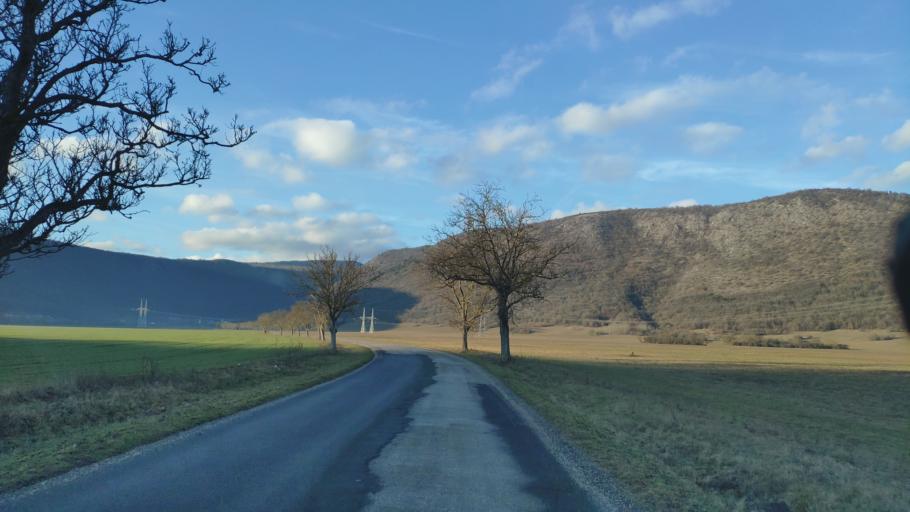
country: SK
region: Kosicky
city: Medzev
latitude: 48.6166
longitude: 20.8783
